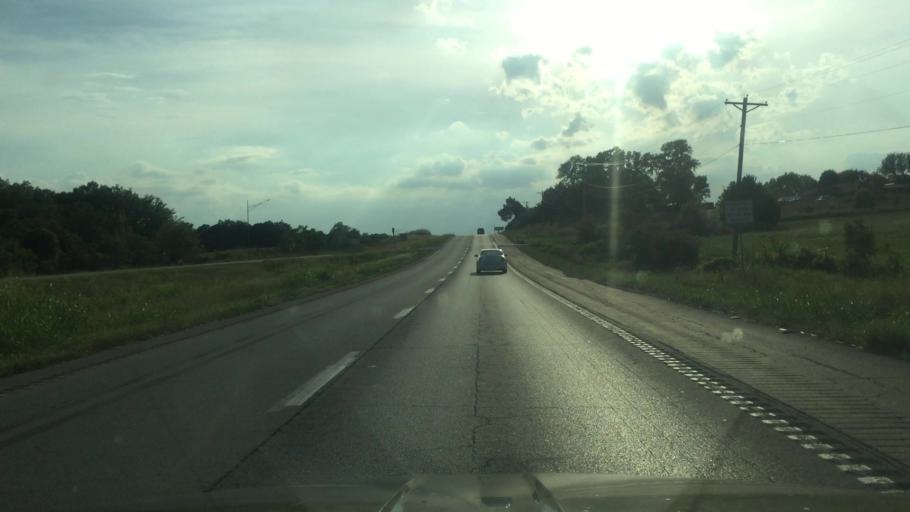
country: US
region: Missouri
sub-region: Jackson County
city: Lone Jack
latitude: 38.8703
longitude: -94.1265
